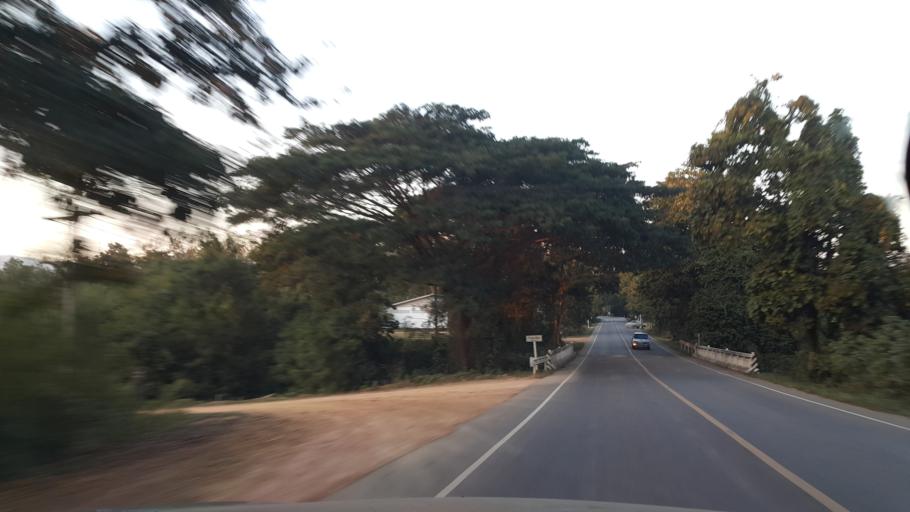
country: TH
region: Phrae
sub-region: Amphoe Wang Chin
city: Wang Chin
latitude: 17.8641
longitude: 99.6223
